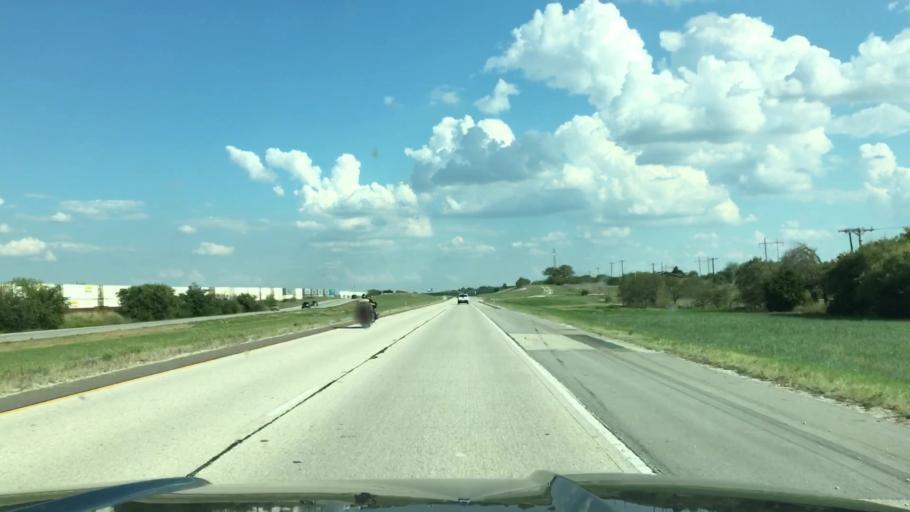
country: US
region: Texas
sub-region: Wise County
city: Decatur
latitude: 33.1653
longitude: -97.5310
